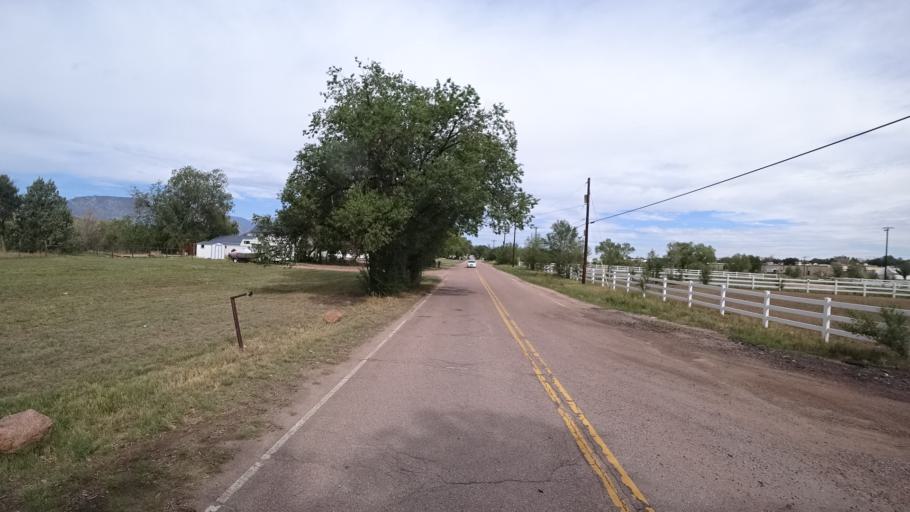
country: US
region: Colorado
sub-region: El Paso County
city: Security-Widefield
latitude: 38.7358
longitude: -104.7350
